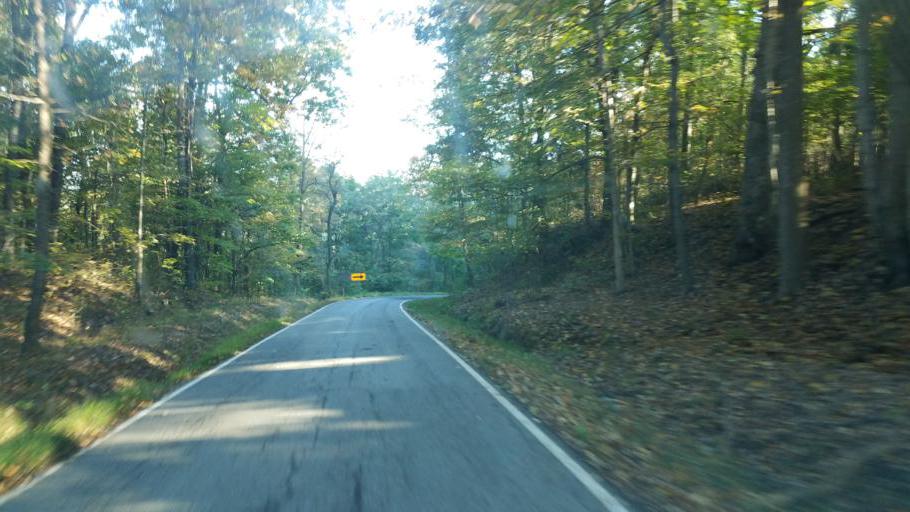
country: US
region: Ohio
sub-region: Adams County
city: Manchester
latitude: 38.5203
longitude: -83.5140
